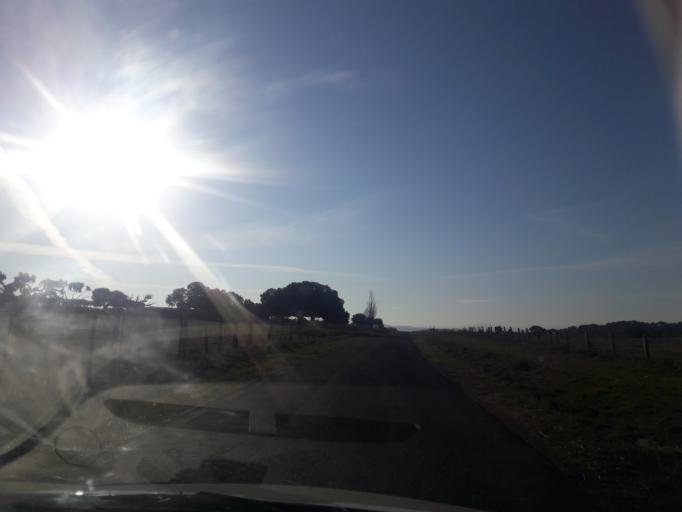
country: ES
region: Castille and Leon
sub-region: Provincia de Salamanca
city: Montejo
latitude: 40.6277
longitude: -5.6174
